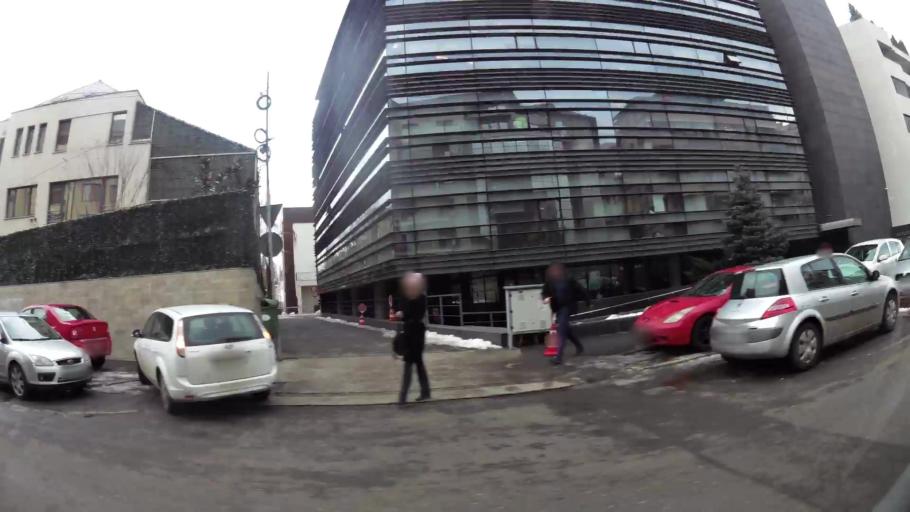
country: RO
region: Bucuresti
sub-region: Municipiul Bucuresti
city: Bucuresti
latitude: 44.4639
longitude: 26.0764
